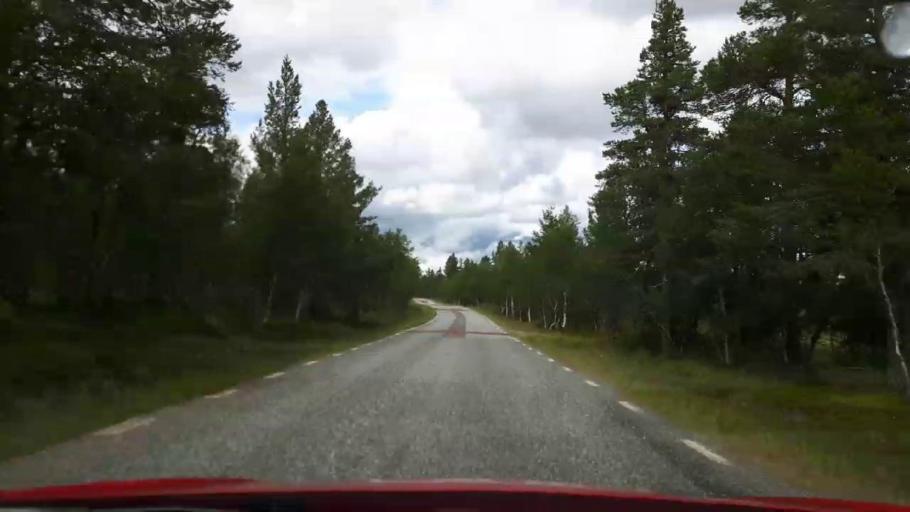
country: NO
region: Hedmark
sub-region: Trysil
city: Innbygda
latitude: 62.1208
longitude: 12.9712
